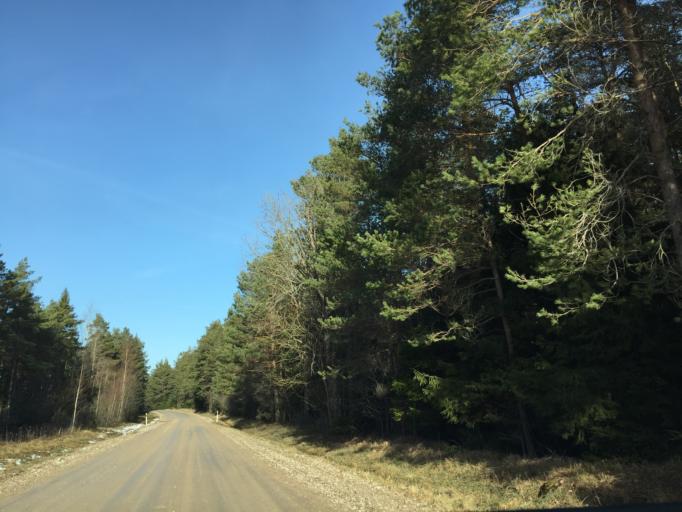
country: EE
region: Saare
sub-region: Kuressaare linn
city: Kuressaare
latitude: 58.3737
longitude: 22.0162
